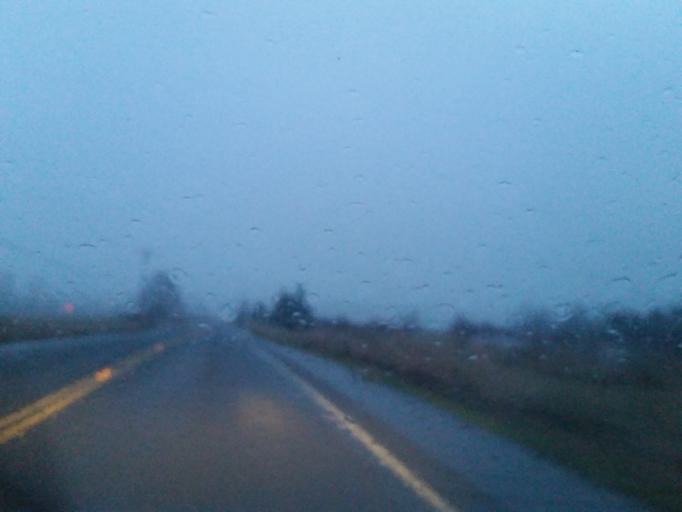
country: US
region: Washington
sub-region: Snohomish County
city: Everett
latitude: 47.9756
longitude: -122.1713
